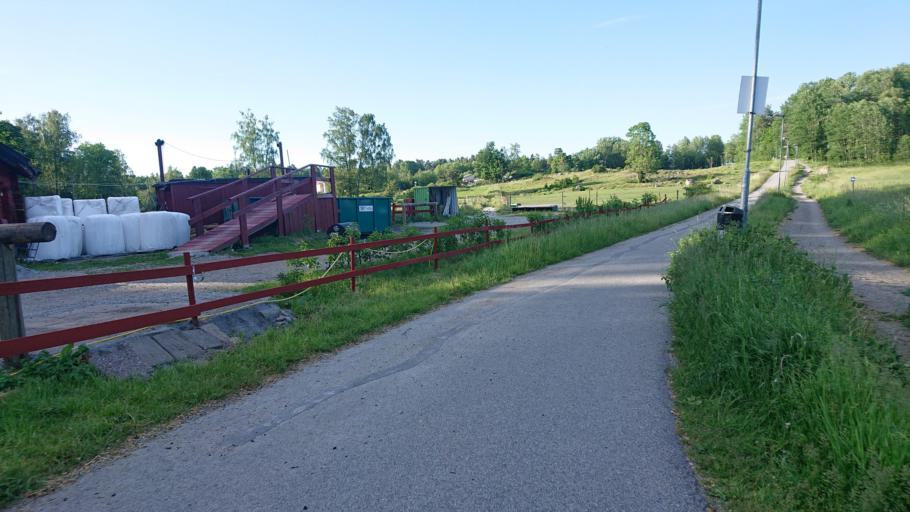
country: SE
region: Stockholm
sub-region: Osterakers Kommun
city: Akersberga
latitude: 59.5010
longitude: 18.2932
